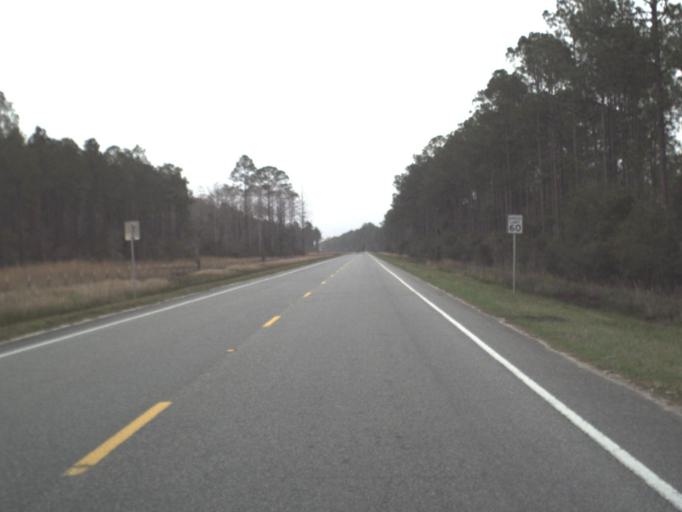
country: US
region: Florida
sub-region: Leon County
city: Woodville
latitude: 30.1978
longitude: -84.1585
